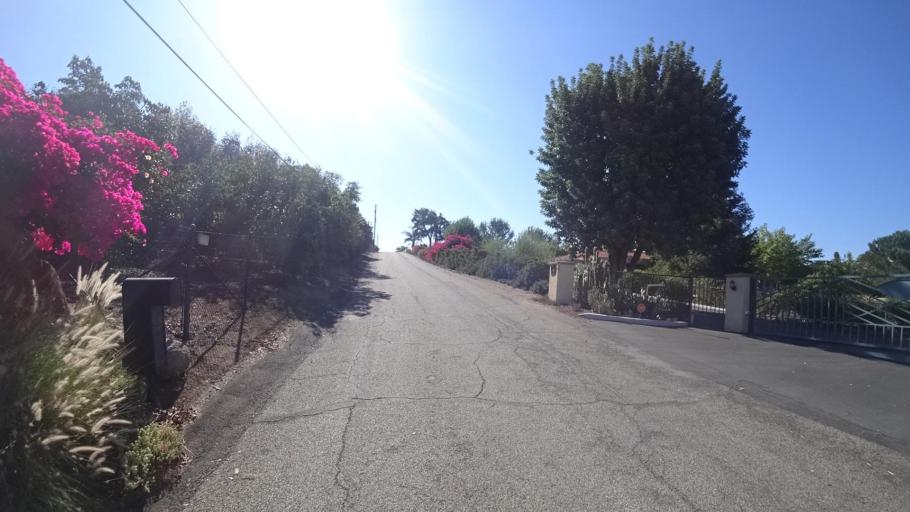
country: US
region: California
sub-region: San Diego County
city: Hidden Meadows
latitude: 33.2309
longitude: -117.1124
